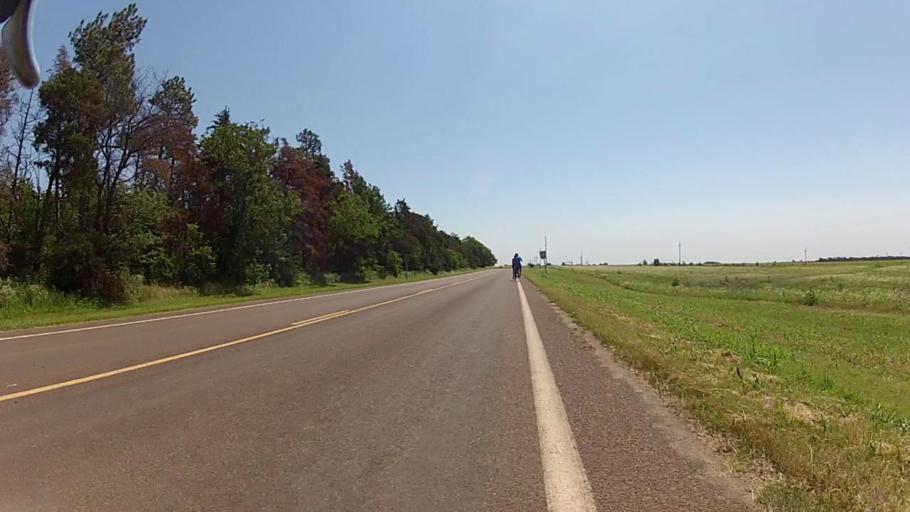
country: US
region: Kansas
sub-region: Sumner County
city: Caldwell
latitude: 37.0326
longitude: -97.5847
